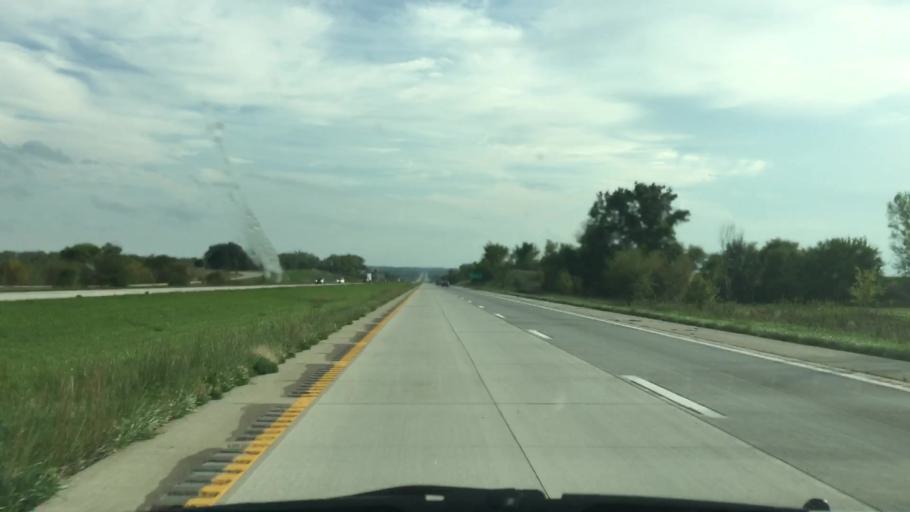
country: US
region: Missouri
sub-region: Daviess County
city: Gallatin
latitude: 40.0670
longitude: -94.0940
